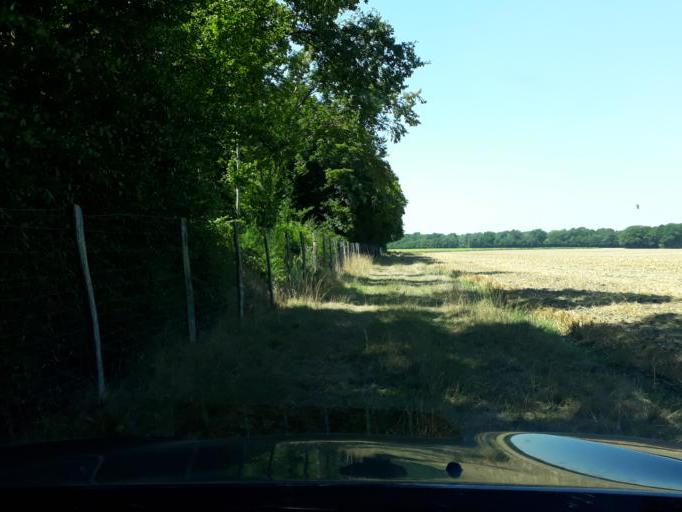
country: FR
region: Centre
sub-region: Departement du Loiret
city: Chevilly
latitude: 47.9952
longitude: 1.9162
